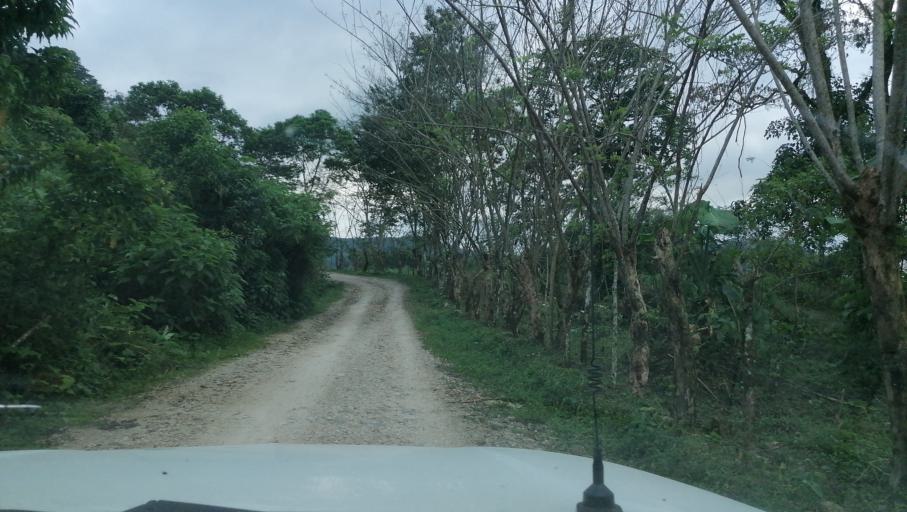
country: MX
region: Chiapas
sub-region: Francisco Leon
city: San Miguel la Sardina
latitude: 17.3030
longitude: -93.2687
